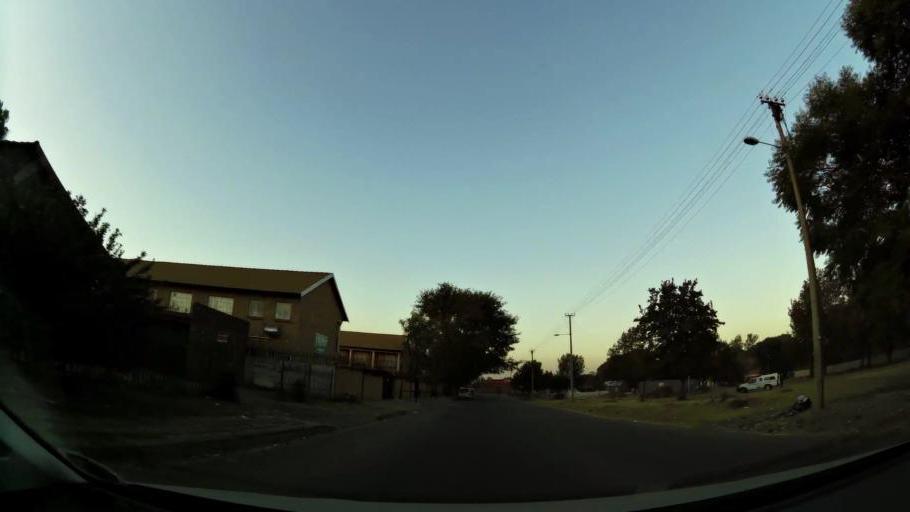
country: ZA
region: North-West
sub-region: Bojanala Platinum District Municipality
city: Rustenburg
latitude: -25.6662
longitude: 27.2485
